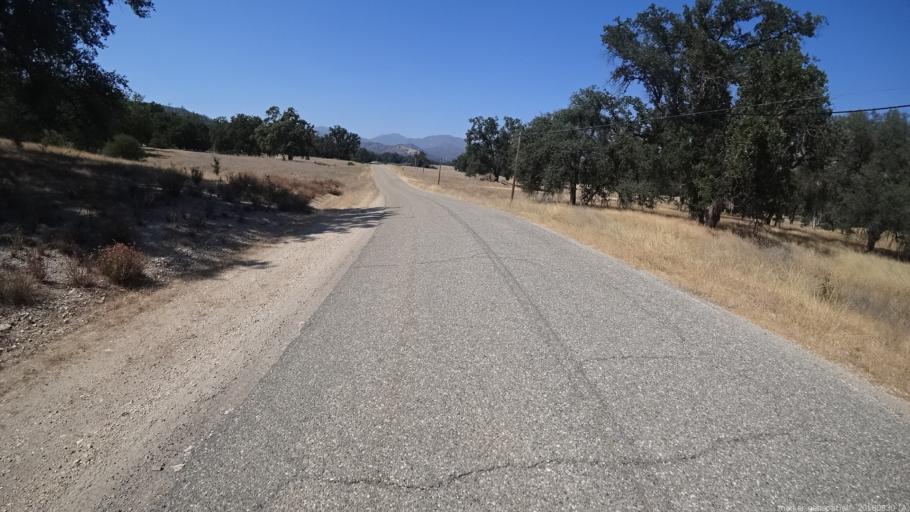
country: US
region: California
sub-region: Monterey County
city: King City
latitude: 36.0418
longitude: -121.2966
